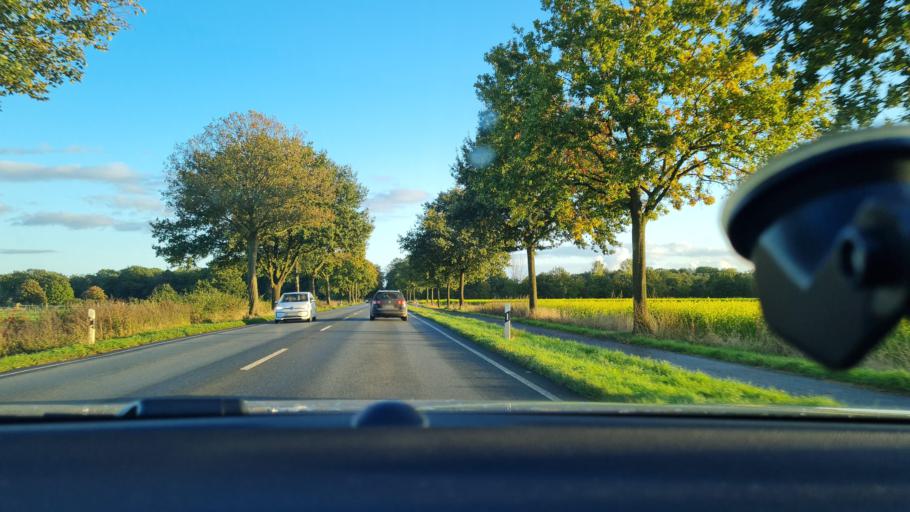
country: DE
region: North Rhine-Westphalia
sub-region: Regierungsbezirk Dusseldorf
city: Voerde
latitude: 51.6108
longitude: 6.6972
